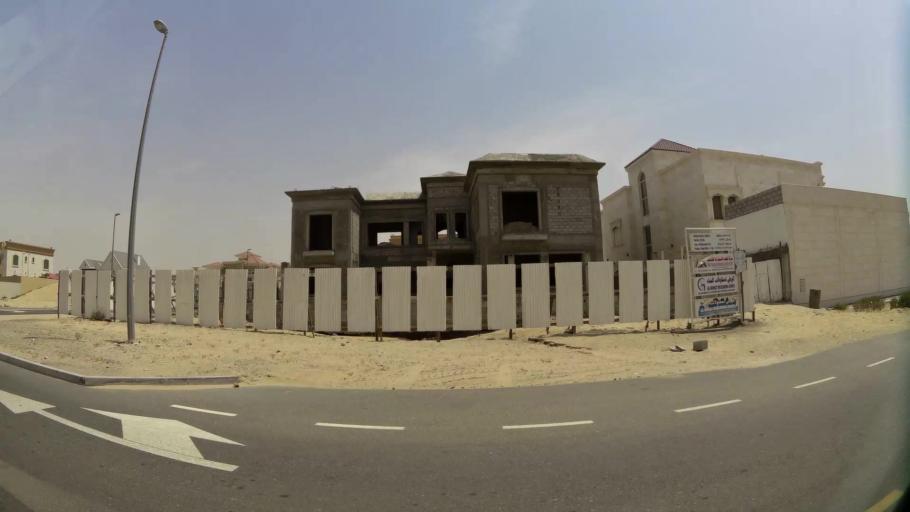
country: AE
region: Ash Shariqah
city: Sharjah
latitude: 25.2524
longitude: 55.5041
